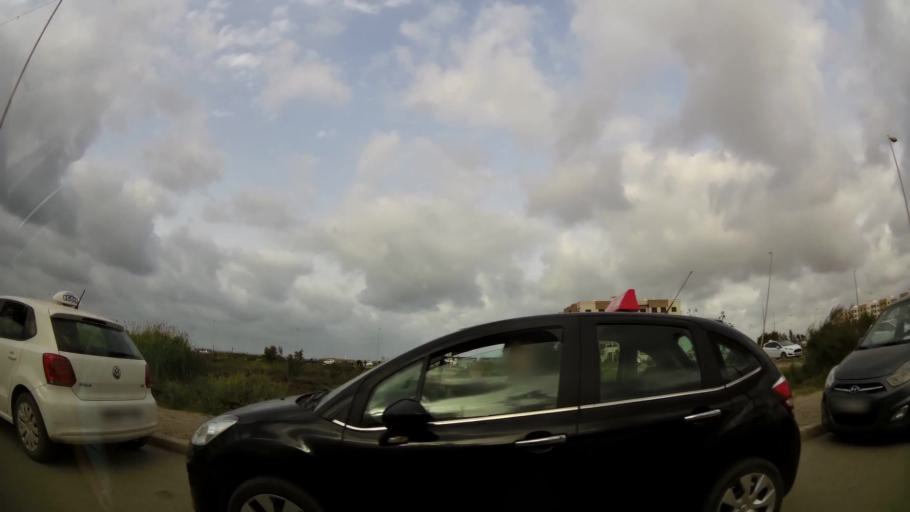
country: MA
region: Oriental
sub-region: Nador
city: Nador
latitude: 35.1550
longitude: -2.9105
